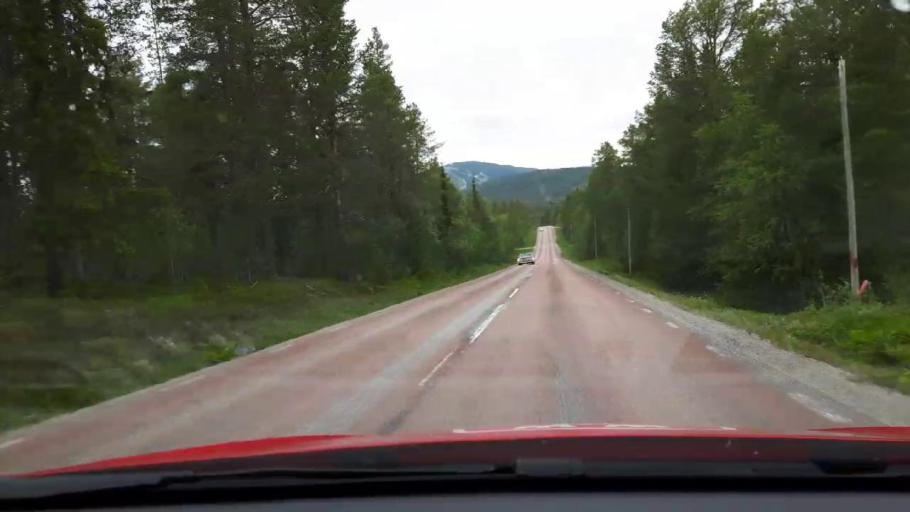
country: NO
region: Hedmark
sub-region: Engerdal
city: Engerdal
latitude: 62.5107
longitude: 12.6082
